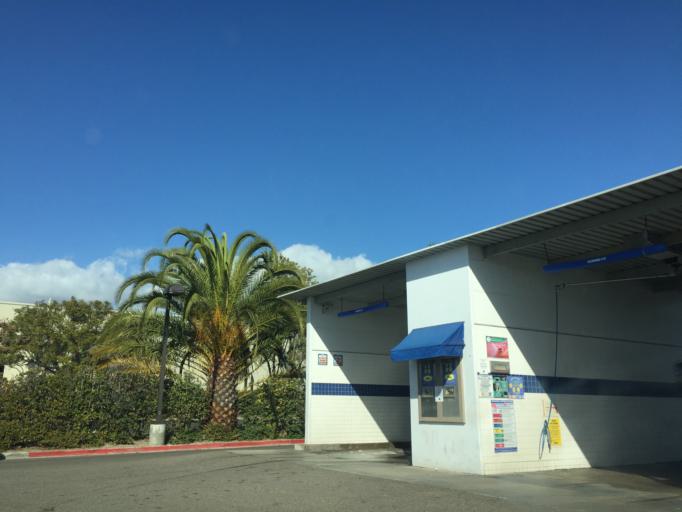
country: US
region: California
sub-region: Santa Barbara County
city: Isla Vista
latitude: 34.4263
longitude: -119.8692
